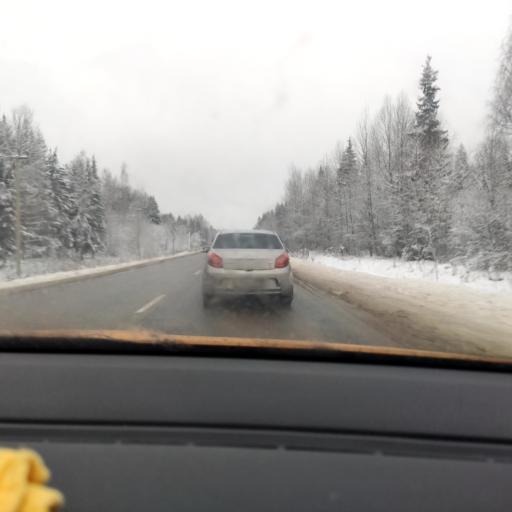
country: RU
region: Moskovskaya
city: Yershovo
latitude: 55.8035
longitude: 36.9507
